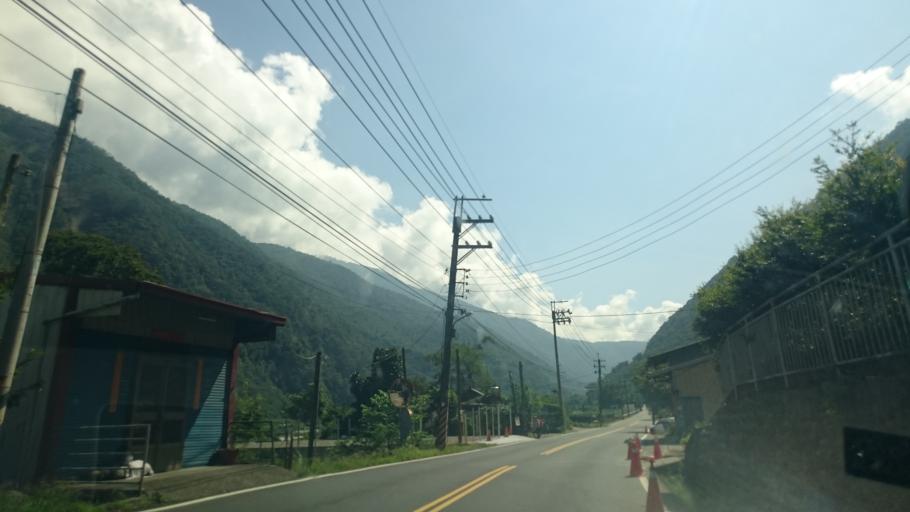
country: TW
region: Taiwan
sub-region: Nantou
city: Puli
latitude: 23.9887
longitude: 121.0207
